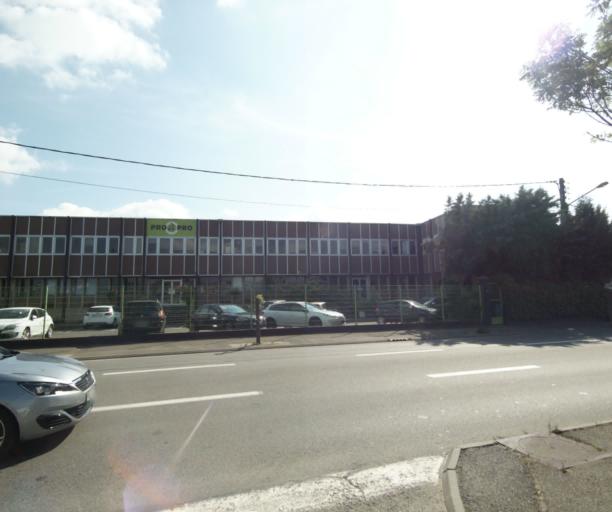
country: FR
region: Midi-Pyrenees
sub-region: Departement du Tarn-et-Garonne
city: Montauban
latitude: 44.0341
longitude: 1.3736
